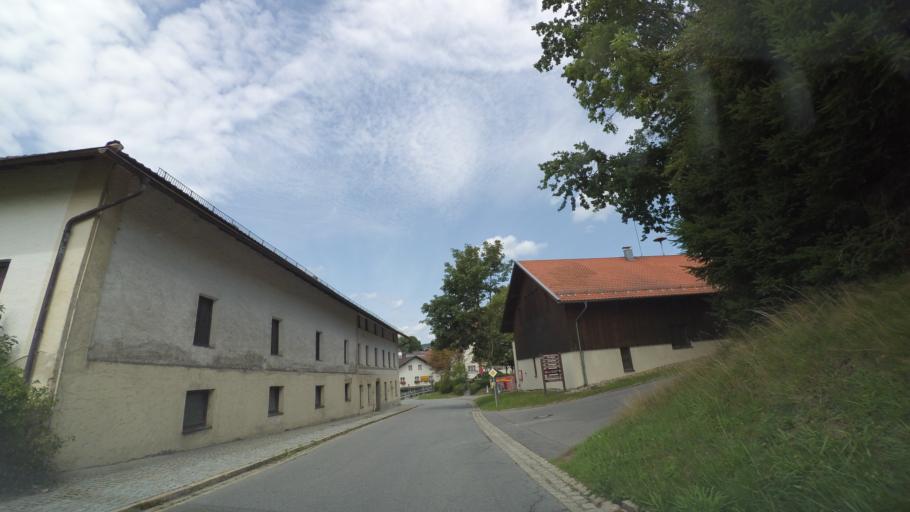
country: DE
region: Bavaria
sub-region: Lower Bavaria
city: Arnbruck
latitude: 49.1278
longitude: 12.9981
